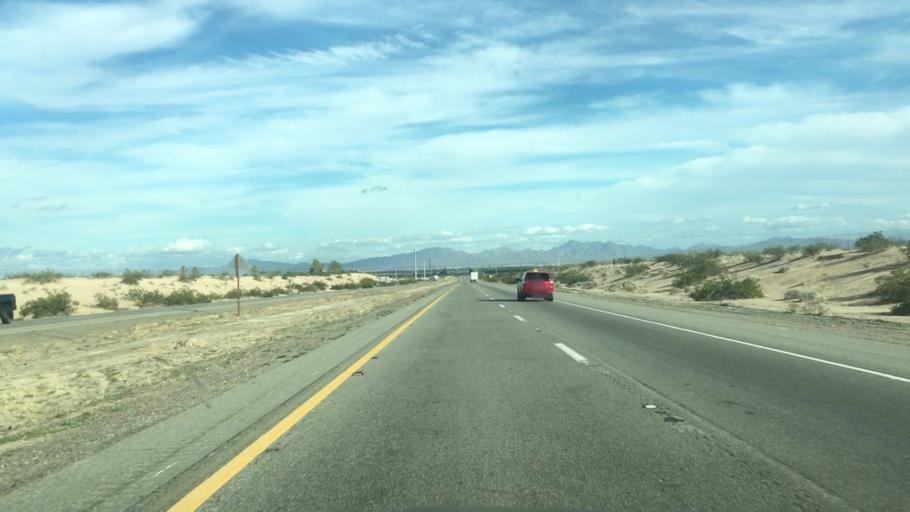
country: US
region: California
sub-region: Riverside County
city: Mesa Verde
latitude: 33.6067
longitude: -114.7083
